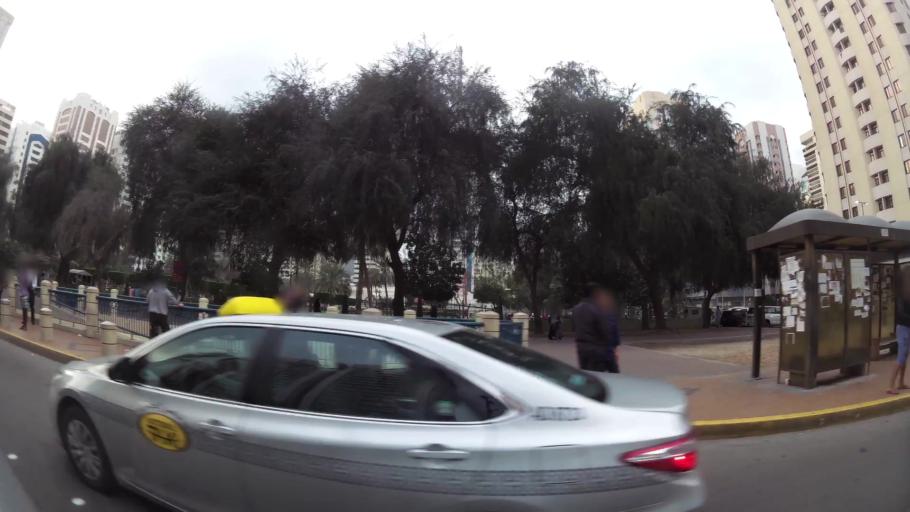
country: AE
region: Abu Dhabi
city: Abu Dhabi
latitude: 24.4962
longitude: 54.3774
